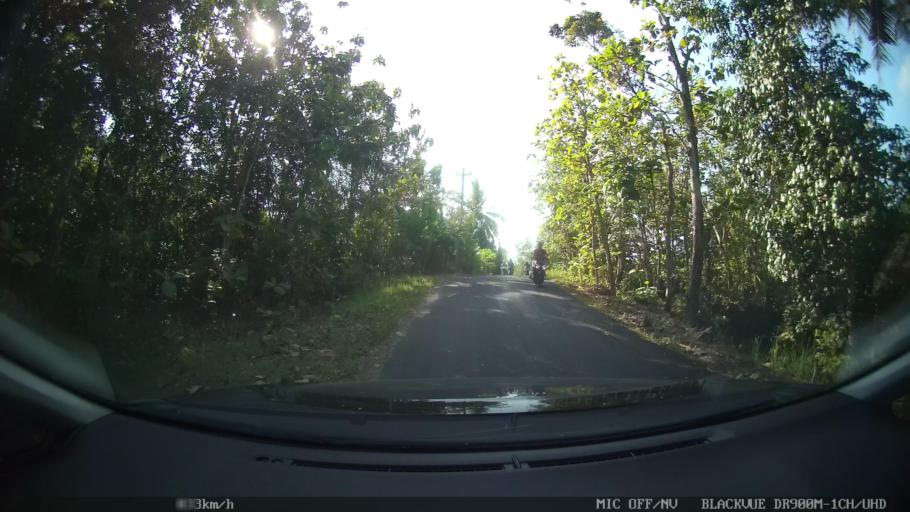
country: ID
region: Daerah Istimewa Yogyakarta
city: Kasihan
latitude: -7.8365
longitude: 110.2849
